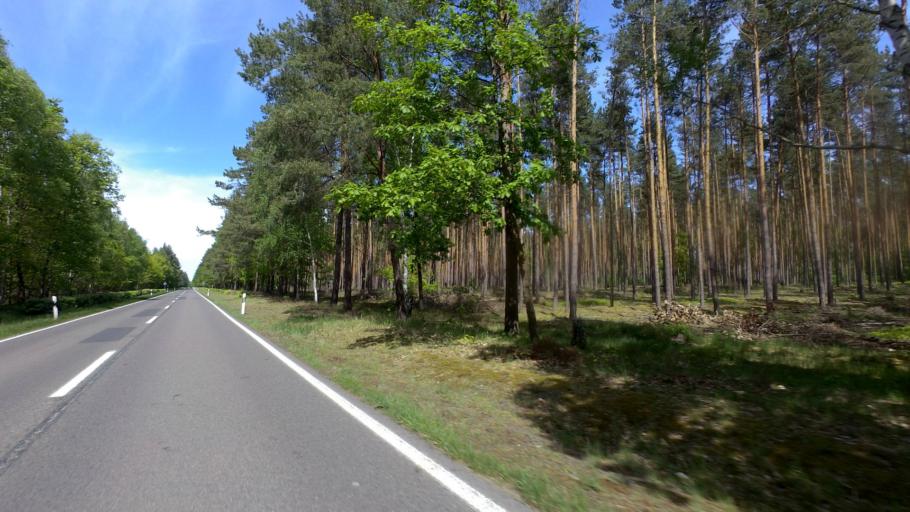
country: DE
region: Brandenburg
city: Sperenberg
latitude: 52.1105
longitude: 13.3713
